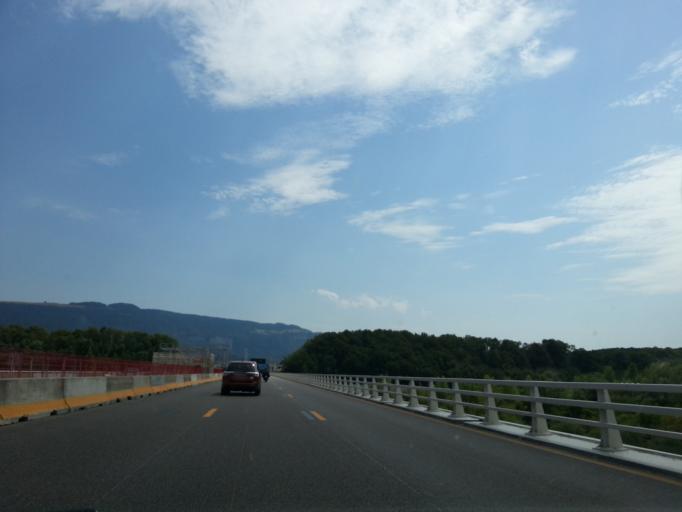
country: FR
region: Rhone-Alpes
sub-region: Departement de la Haute-Savoie
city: Saint-Julien-en-Genevois
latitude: 46.1451
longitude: 6.0963
